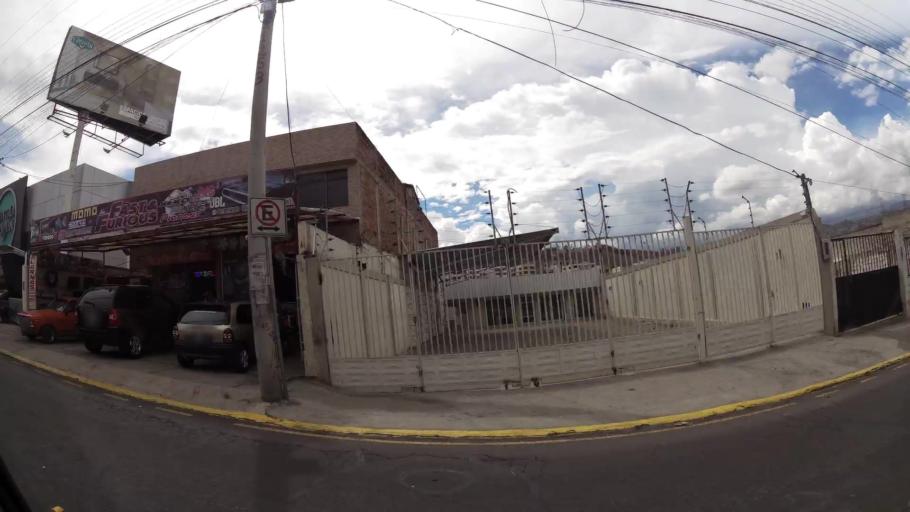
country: EC
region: Tungurahua
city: Ambato
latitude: -1.2715
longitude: -78.6295
